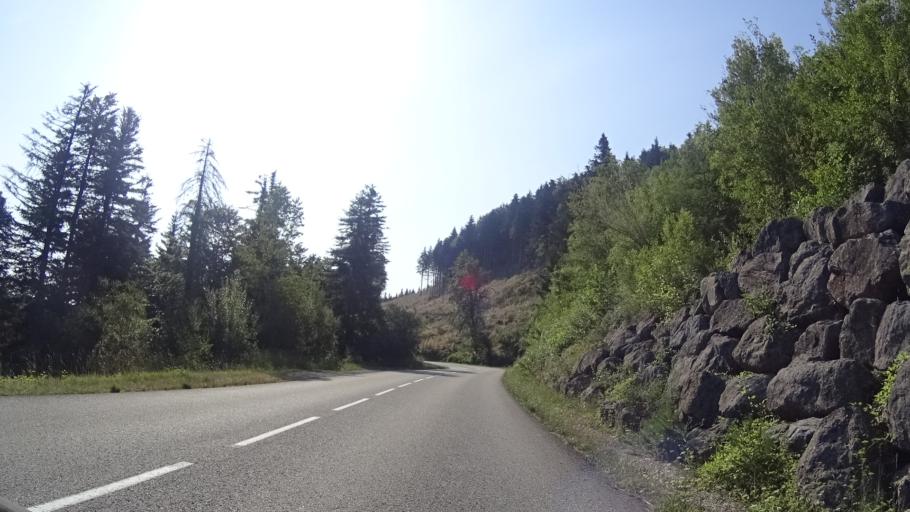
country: FR
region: Midi-Pyrenees
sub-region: Departement de l'Ariege
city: Belesta
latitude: 42.9112
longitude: 1.9964
